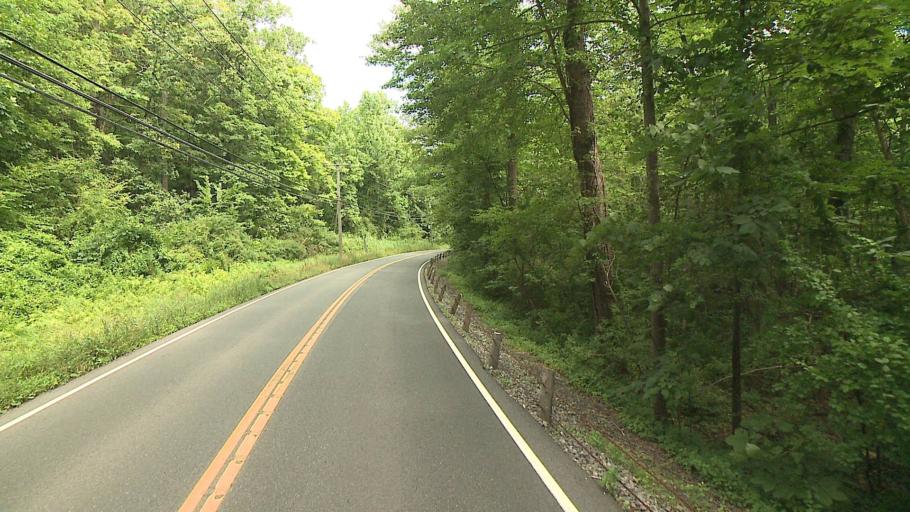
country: US
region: Connecticut
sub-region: Fairfield County
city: Sherman
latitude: 41.5005
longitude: -73.4701
